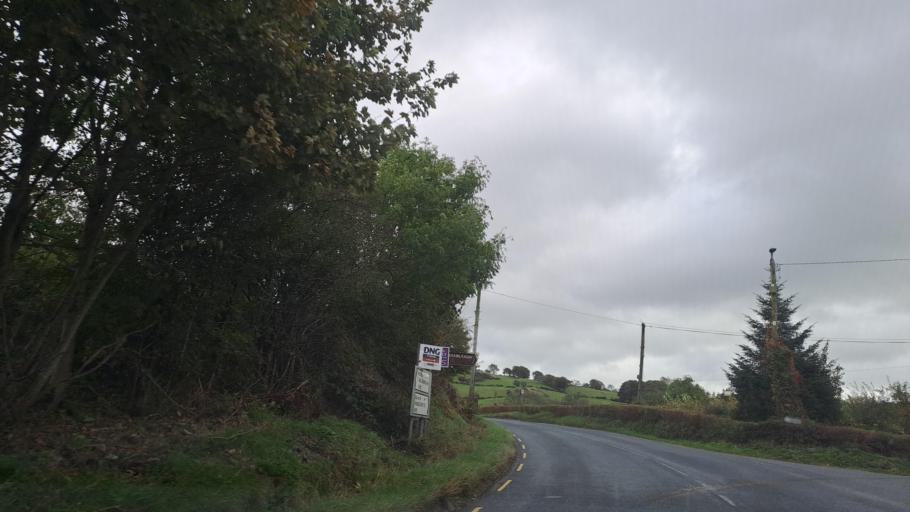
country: IE
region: Ulster
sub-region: An Cabhan
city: Bailieborough
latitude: 53.9187
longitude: -6.9568
